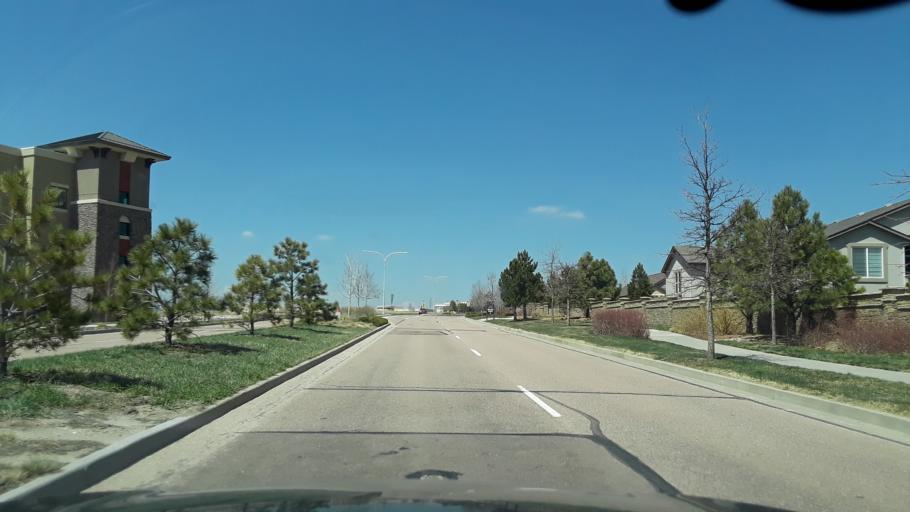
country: US
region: Colorado
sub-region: El Paso County
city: Black Forest
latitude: 38.9638
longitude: -104.7332
